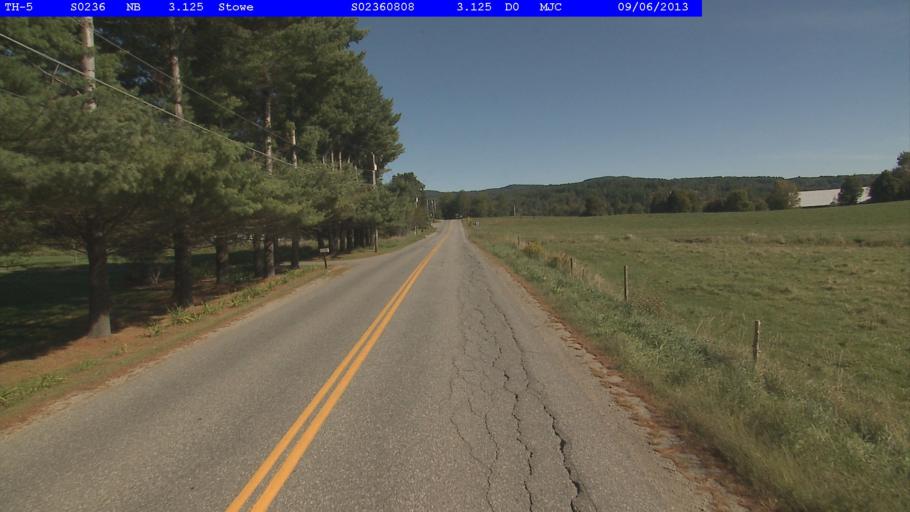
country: US
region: Vermont
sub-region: Washington County
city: Waterbury
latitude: 44.4696
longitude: -72.7272
